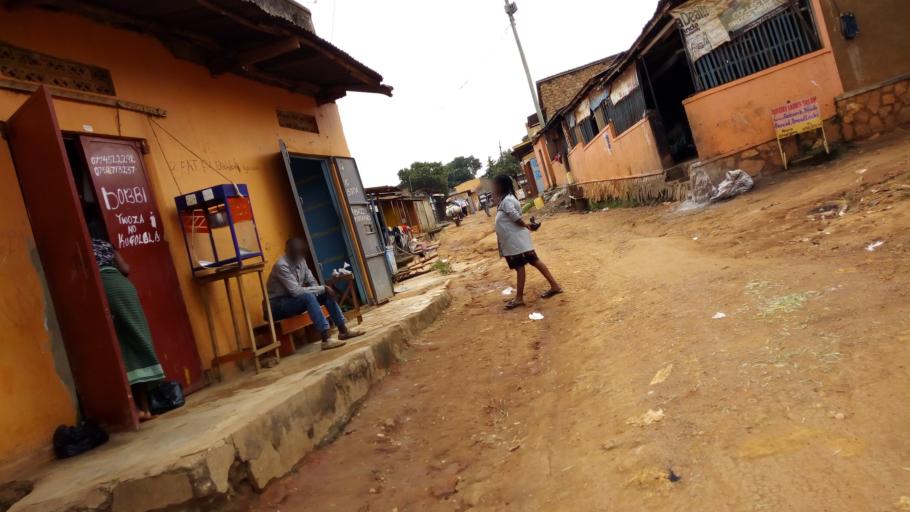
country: UG
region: Central Region
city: Kampala Central Division
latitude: 0.3789
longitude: 32.5602
